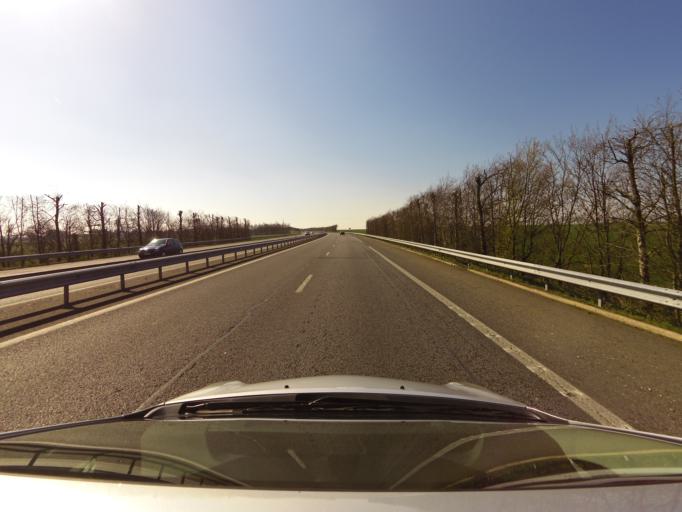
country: FR
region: Brittany
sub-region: Departement d'Ille-et-Vilaine
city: Plelan-le-Grand
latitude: 47.9773
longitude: -2.0981
